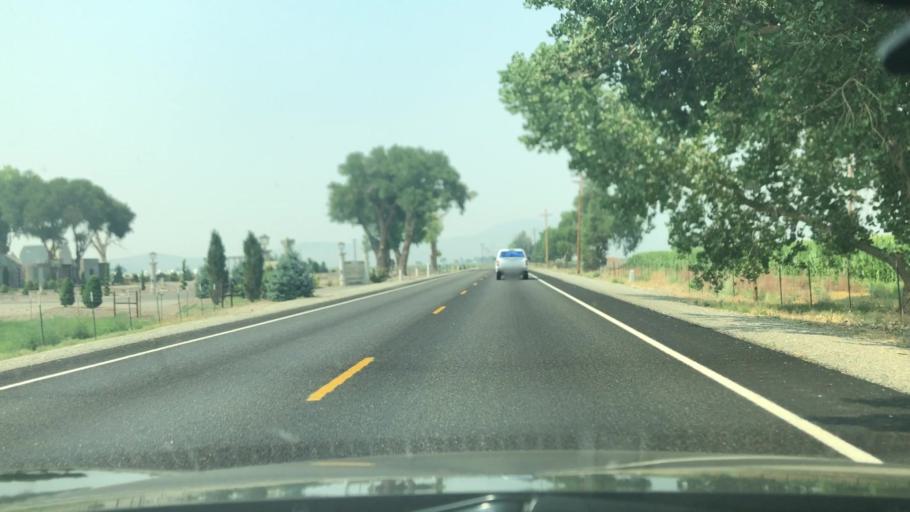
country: US
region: Nevada
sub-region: Lyon County
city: Yerington
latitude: 39.1158
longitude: -119.1810
